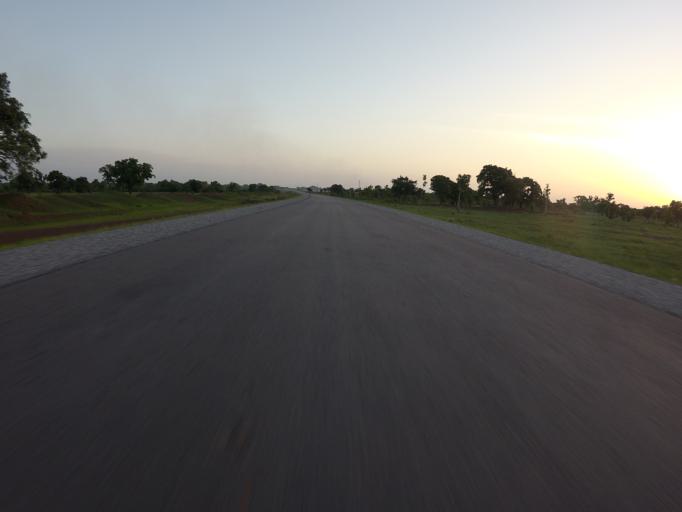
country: GH
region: Northern
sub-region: Yendi
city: Yendi
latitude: 9.9608
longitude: -0.1454
